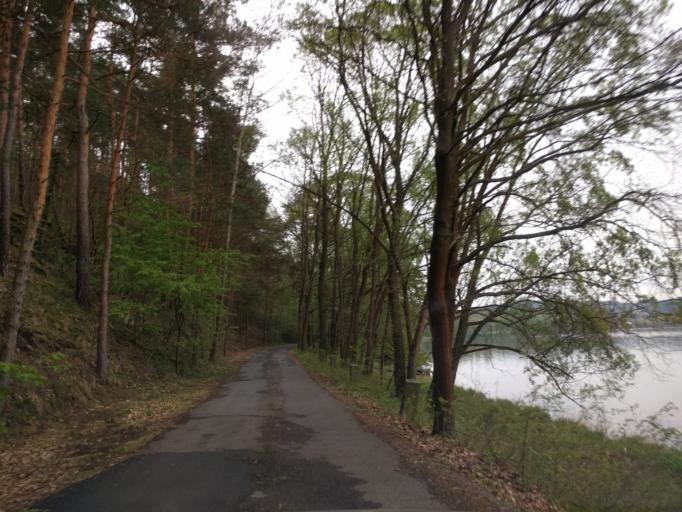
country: CZ
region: Central Bohemia
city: Krasna Hora nad Vltavou
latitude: 49.6724
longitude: 14.2635
